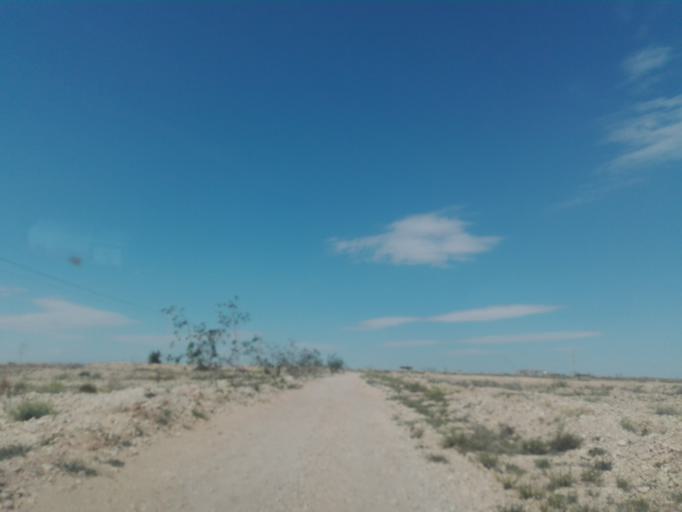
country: TN
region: Safaqis
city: Sfax
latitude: 34.6876
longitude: 10.5422
